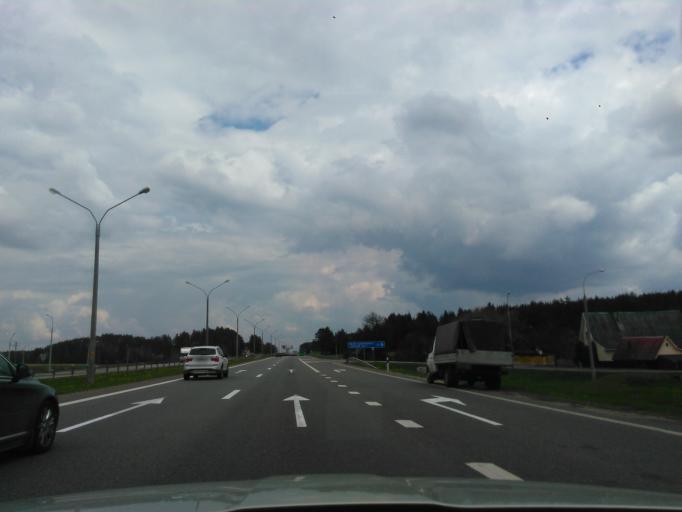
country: BY
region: Minsk
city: Korolev Stan
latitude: 53.9756
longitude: 27.7655
